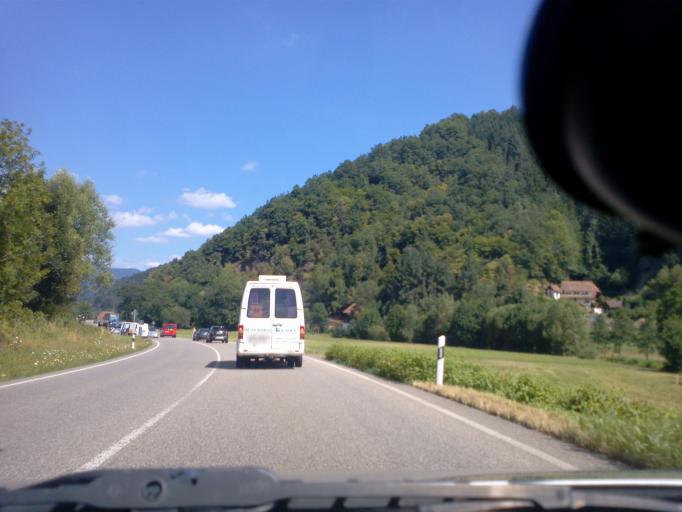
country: DE
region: Baden-Wuerttemberg
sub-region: Freiburg Region
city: Gutach (Schwarzwaldbahn)
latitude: 48.2585
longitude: 8.2090
